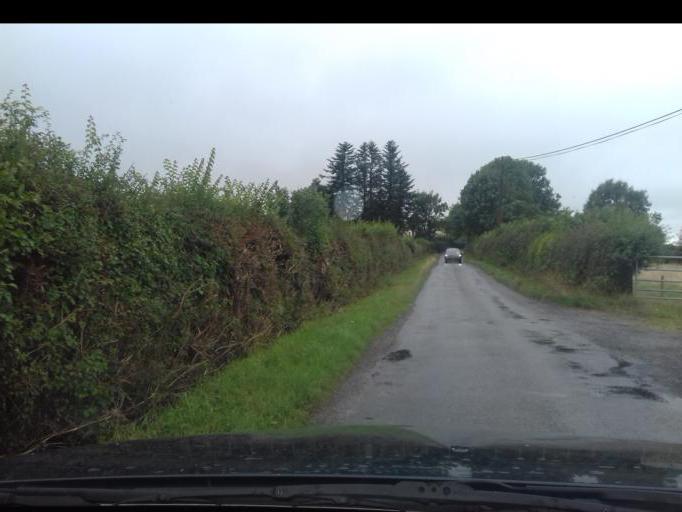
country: IE
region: Leinster
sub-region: Kilkenny
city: Graiguenamanagh
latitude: 52.5812
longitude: -6.9377
